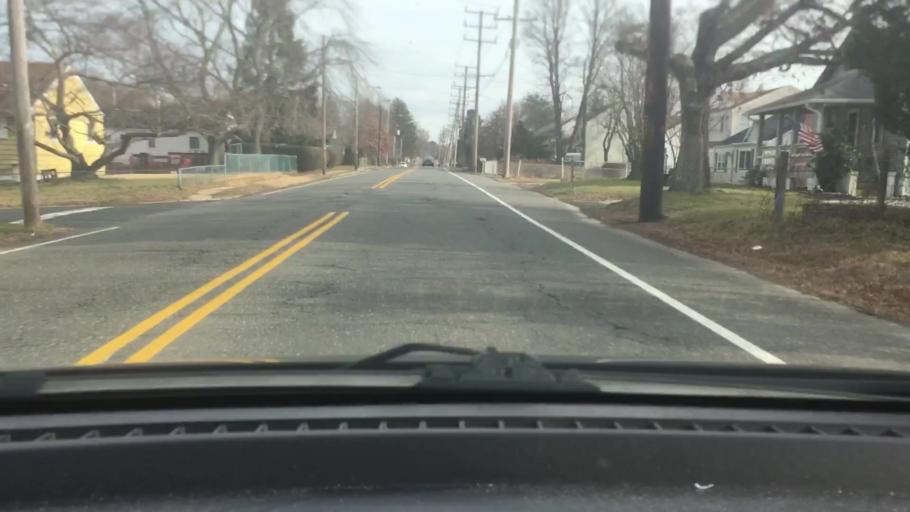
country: US
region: New Jersey
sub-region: Monmouth County
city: Shark River Hills
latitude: 40.2183
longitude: -74.0669
